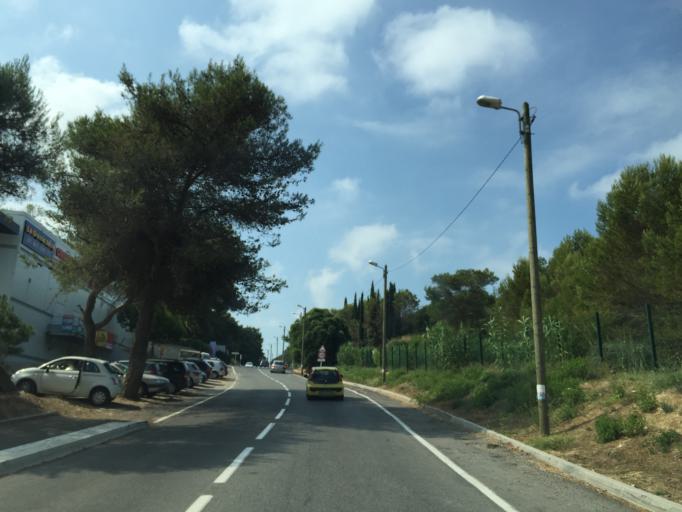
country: FR
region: Provence-Alpes-Cote d'Azur
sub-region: Departement des Alpes-Maritimes
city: Vallauris
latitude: 43.6012
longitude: 7.0760
